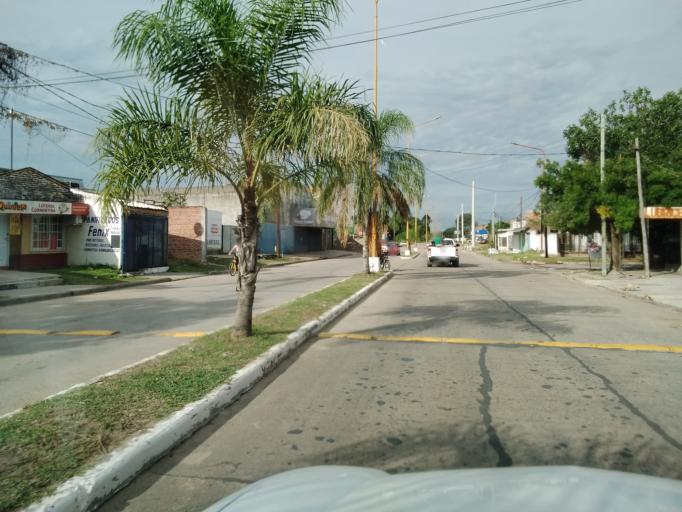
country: AR
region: Corrientes
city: Corrientes
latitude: -27.4611
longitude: -58.7819
